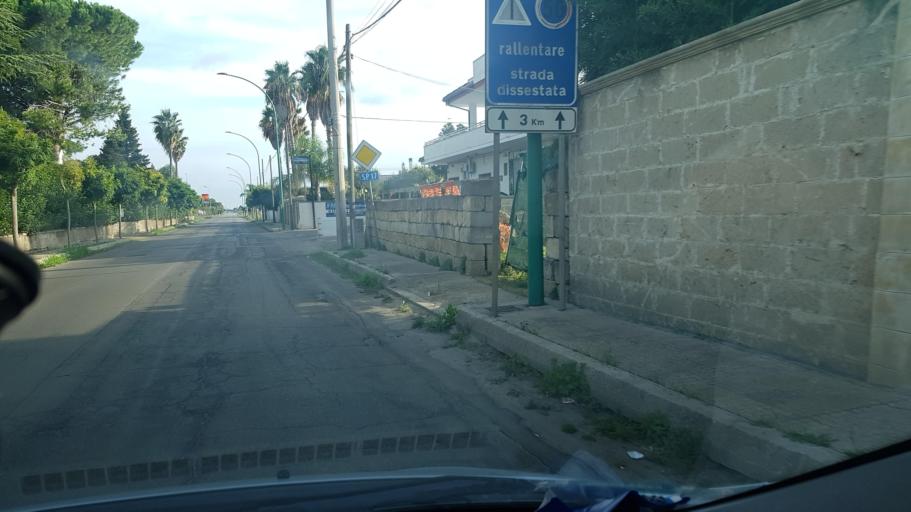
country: IT
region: Apulia
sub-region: Provincia di Lecce
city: Veglie
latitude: 40.3299
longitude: 17.9735
